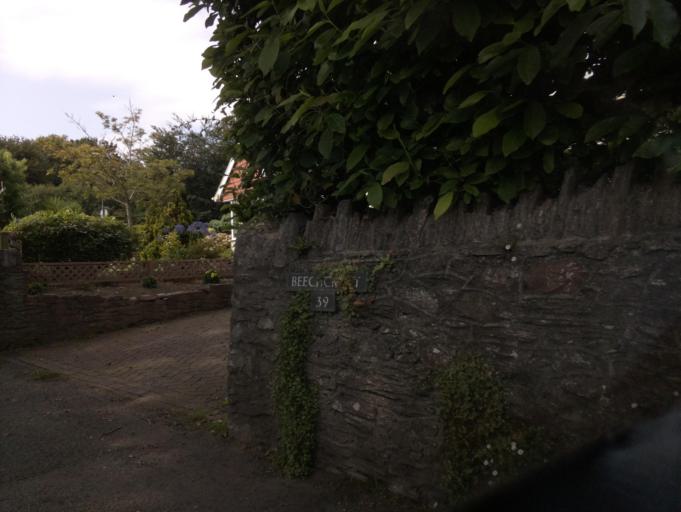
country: GB
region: England
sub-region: Borough of Torbay
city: Brixham
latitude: 50.3882
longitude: -3.5232
